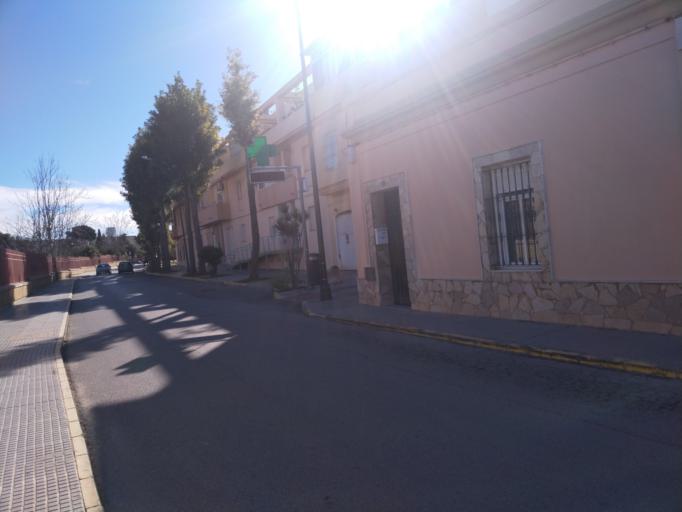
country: ES
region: Andalusia
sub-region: Provincia de Cadiz
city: San Fernando
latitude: 36.4799
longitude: -6.1963
